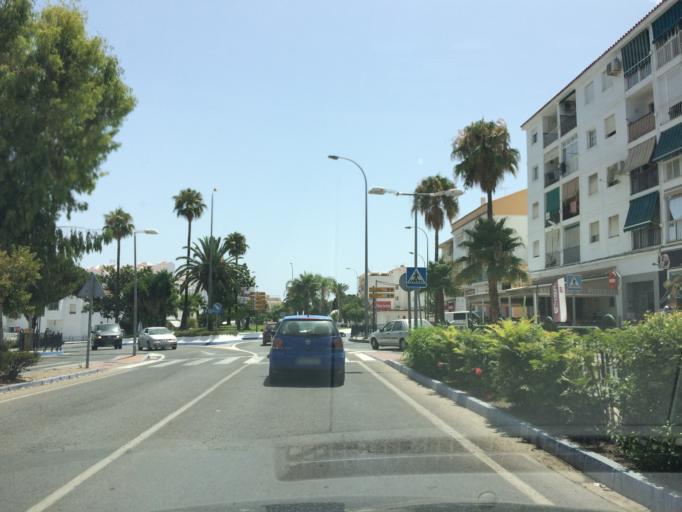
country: ES
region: Andalusia
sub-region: Provincia de Malaga
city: Nerja
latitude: 36.7540
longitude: -3.8748
